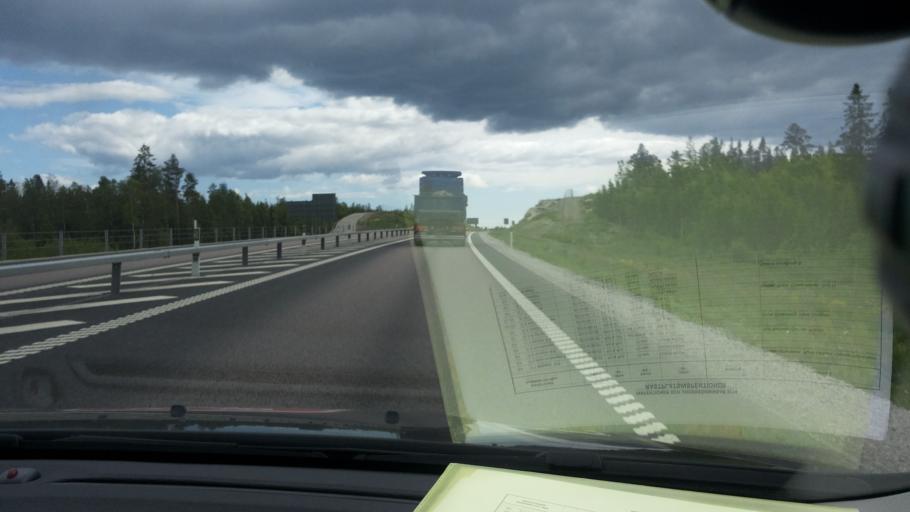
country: SE
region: Vaesternorrland
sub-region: Sundsvalls Kommun
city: Njurundabommen
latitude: 62.2614
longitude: 17.3624
